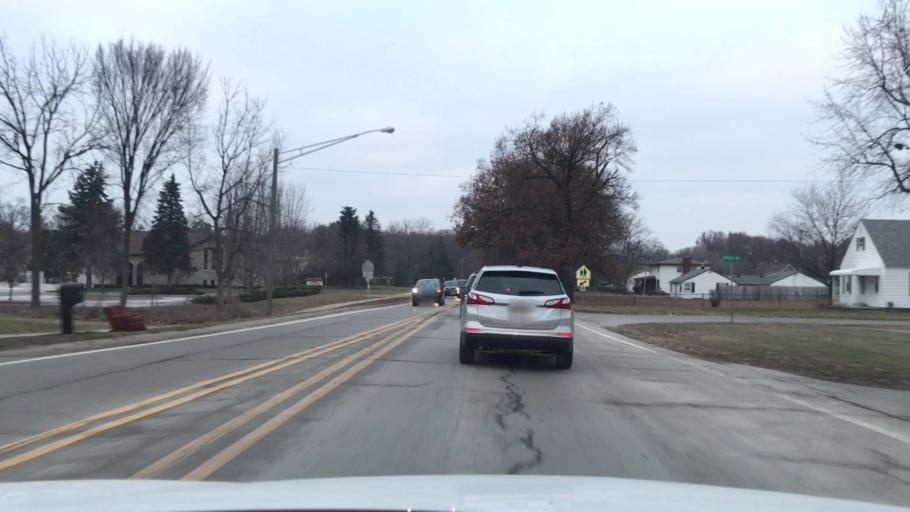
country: US
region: Michigan
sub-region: Oakland County
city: Waterford
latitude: 42.6923
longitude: -83.3729
